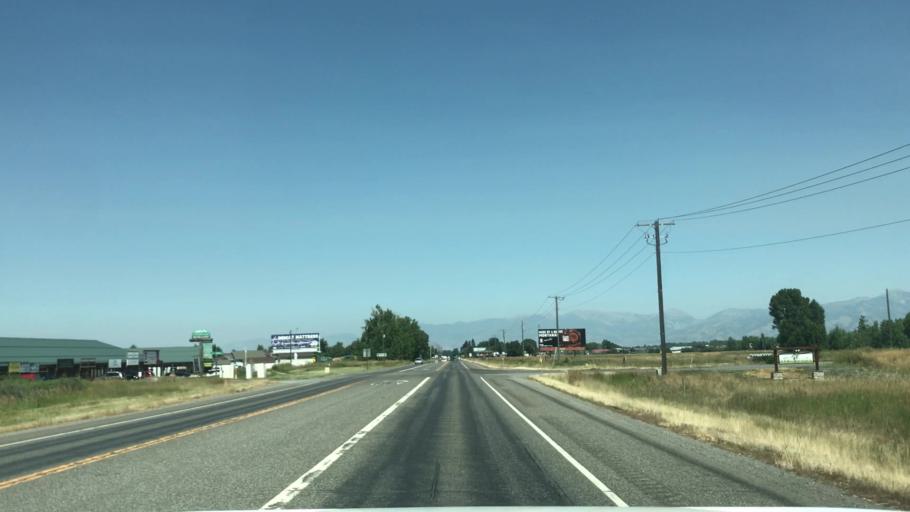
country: US
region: Montana
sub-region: Gallatin County
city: Four Corners
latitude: 45.6450
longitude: -111.1946
